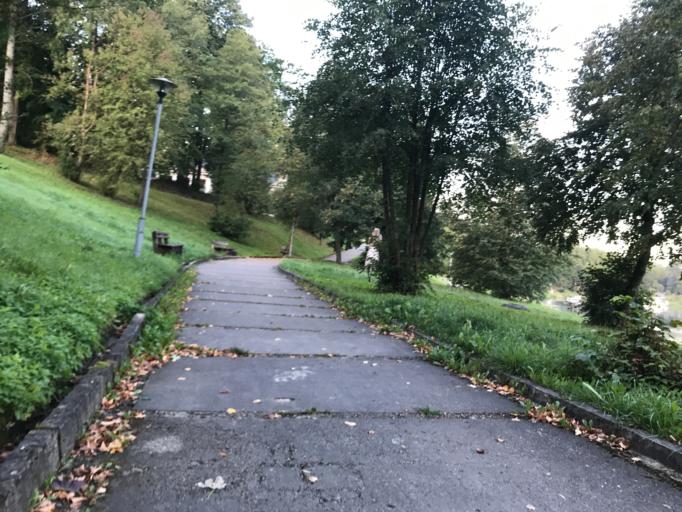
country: LT
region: Alytaus apskritis
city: Druskininkai
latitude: 54.0188
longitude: 23.9864
